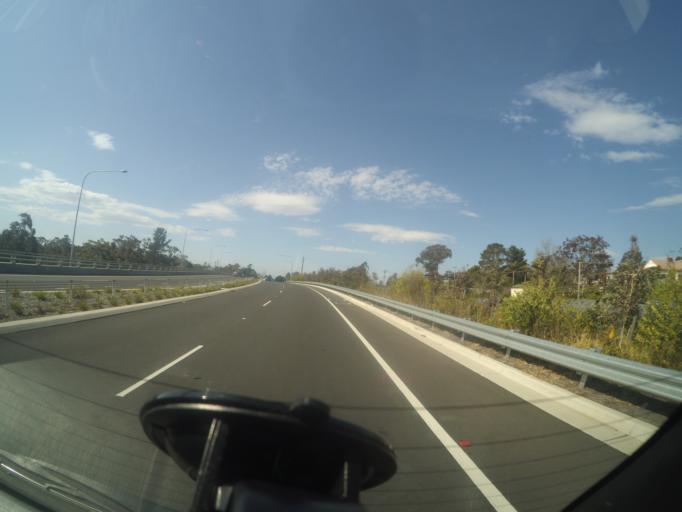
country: AU
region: New South Wales
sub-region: Blue Mountains Municipality
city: Hazelbrook
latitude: -33.7338
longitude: 150.4689
